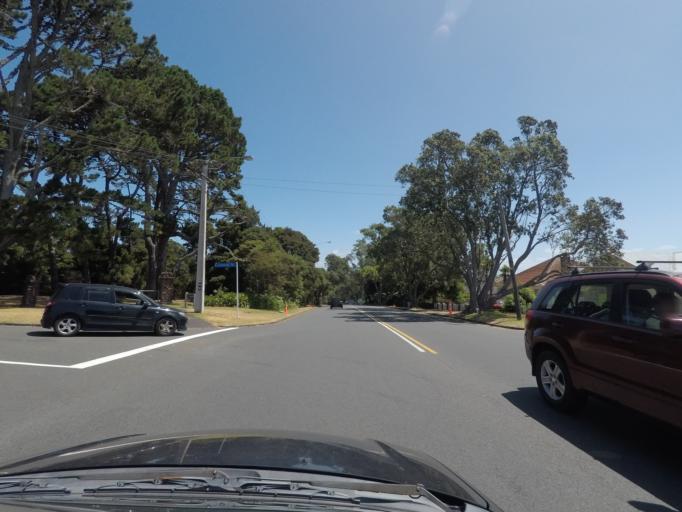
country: NZ
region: Auckland
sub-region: Auckland
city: Waitakere
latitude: -36.9252
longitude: 174.6940
